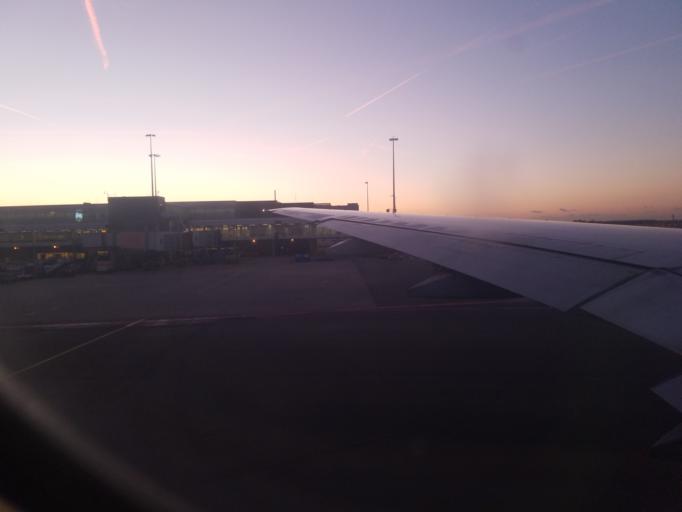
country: NL
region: North Holland
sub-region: Gemeente Aalsmeer
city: Aalsmeer
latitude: 52.3143
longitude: 4.7589
